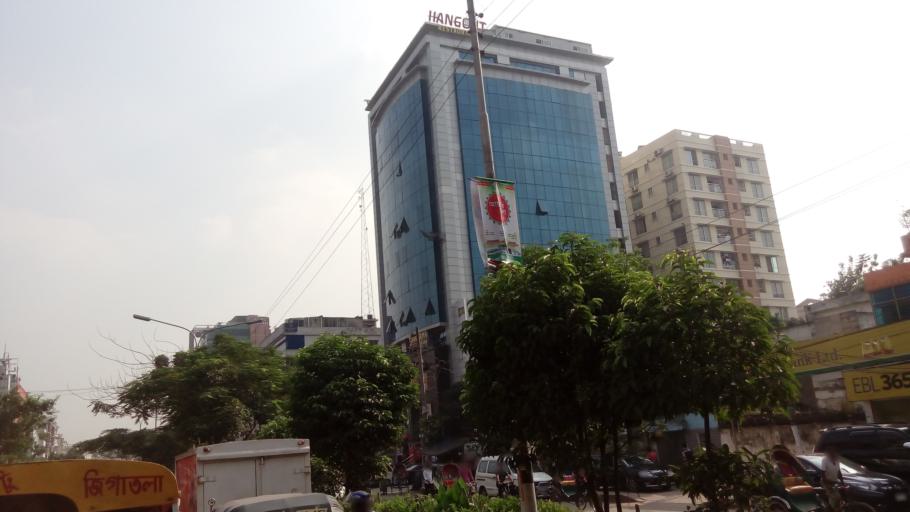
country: BD
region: Dhaka
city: Azimpur
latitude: 23.7467
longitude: 90.3710
